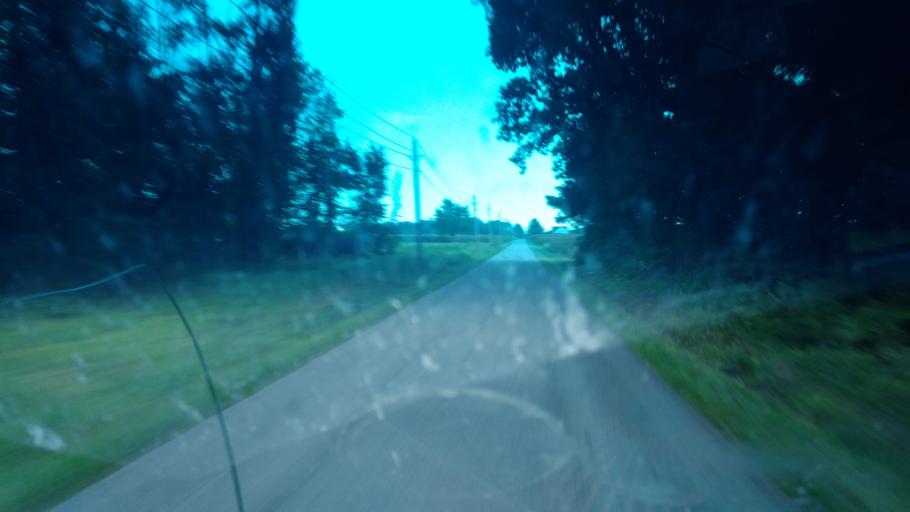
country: US
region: Ohio
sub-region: Crawford County
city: Galion
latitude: 40.7928
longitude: -82.8192
